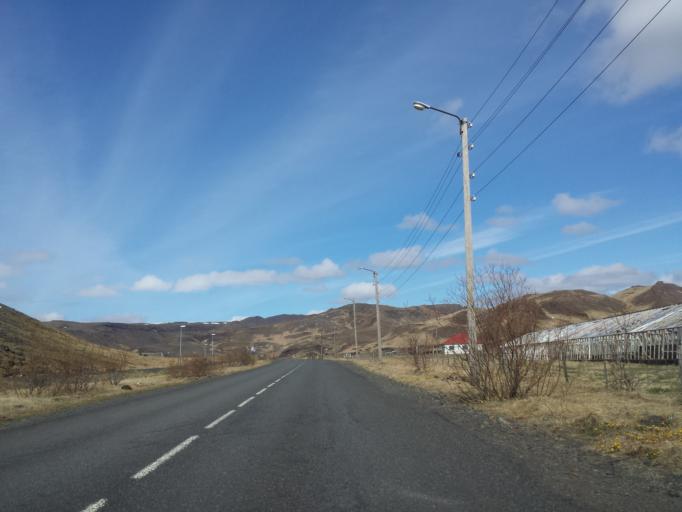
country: IS
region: South
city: Hveragerdi
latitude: 64.0084
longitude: -21.1883
